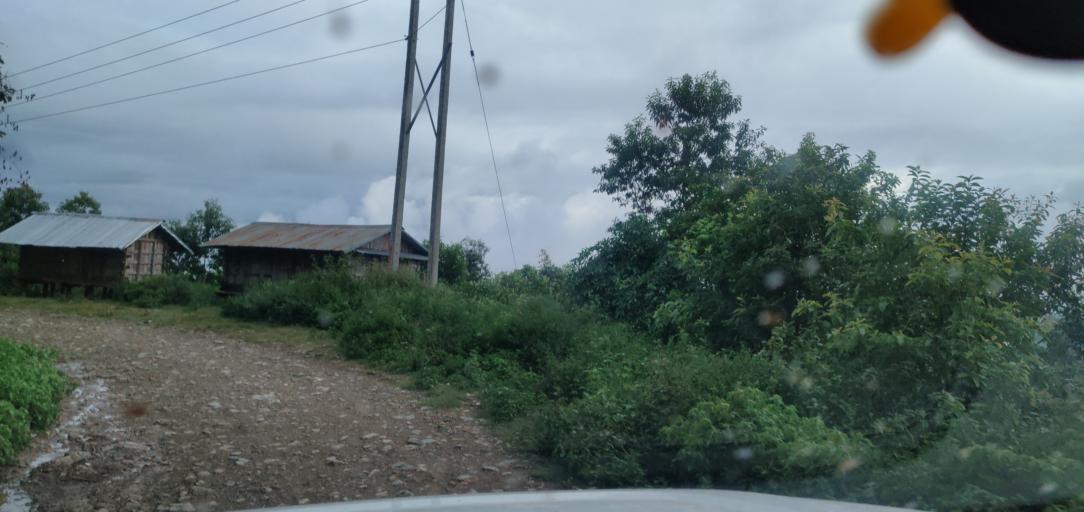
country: LA
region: Phongsali
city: Phongsali
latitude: 21.4415
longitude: 102.2942
